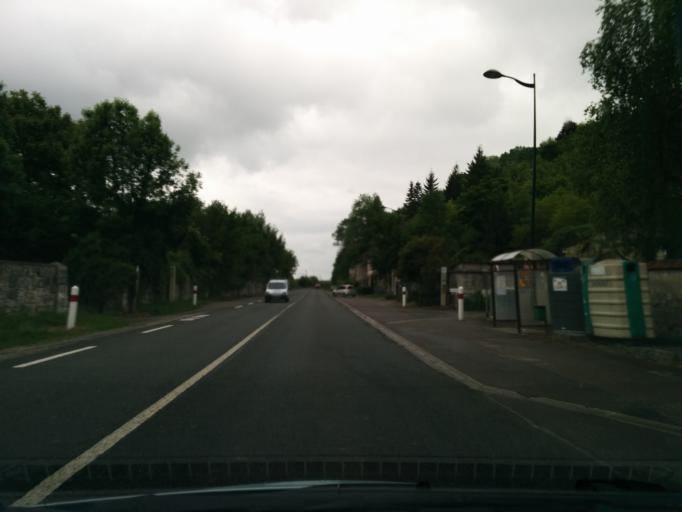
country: FR
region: Ile-de-France
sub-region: Departement des Yvelines
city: Limetz-Villez
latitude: 49.0741
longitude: 1.5124
